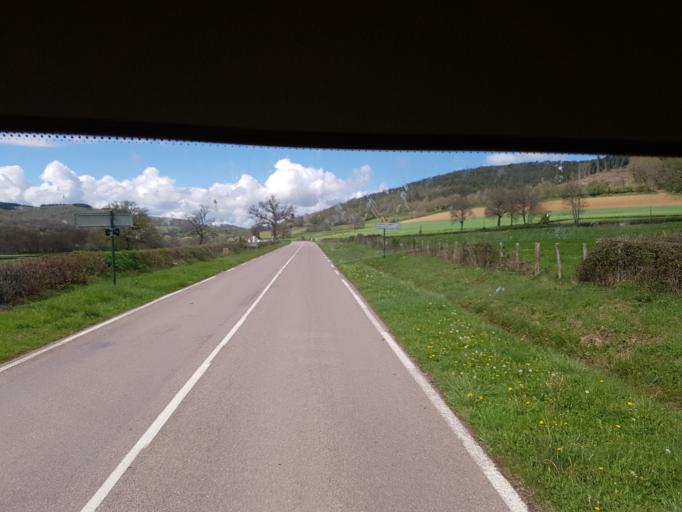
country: FR
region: Bourgogne
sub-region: Departement de Saone-et-Loire
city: Autun
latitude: 47.0891
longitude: 4.2395
